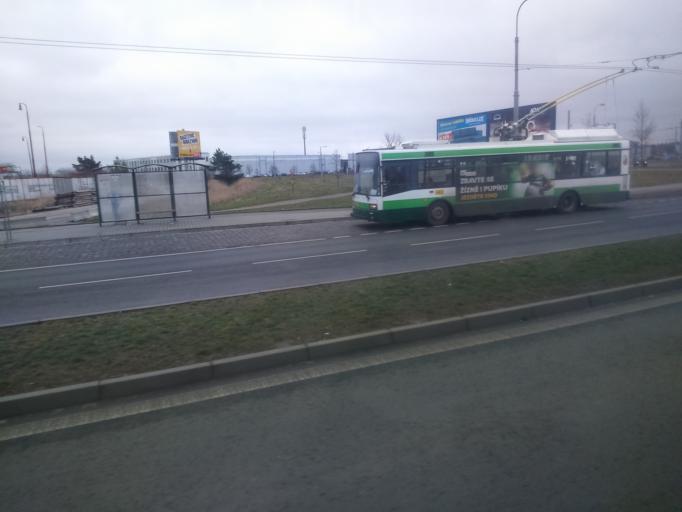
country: CZ
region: Plzensky
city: Vejprnice
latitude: 49.7326
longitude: 13.3217
